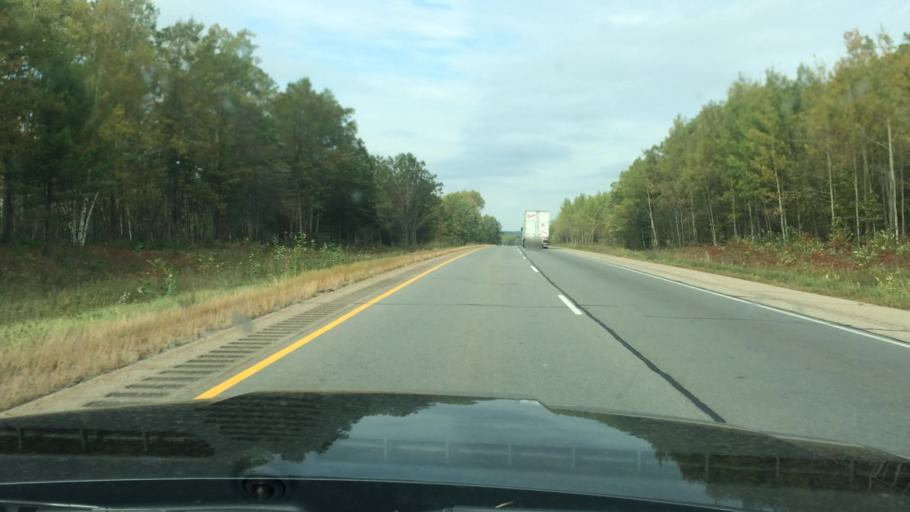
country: US
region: Wisconsin
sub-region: Marathon County
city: Mosinee
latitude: 44.7045
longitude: -89.6531
